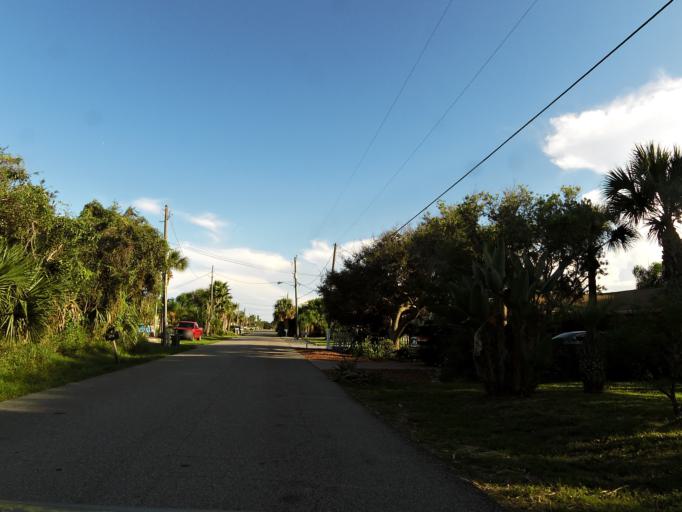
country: US
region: Florida
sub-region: Flagler County
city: Flagler Beach
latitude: 29.4547
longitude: -81.1172
